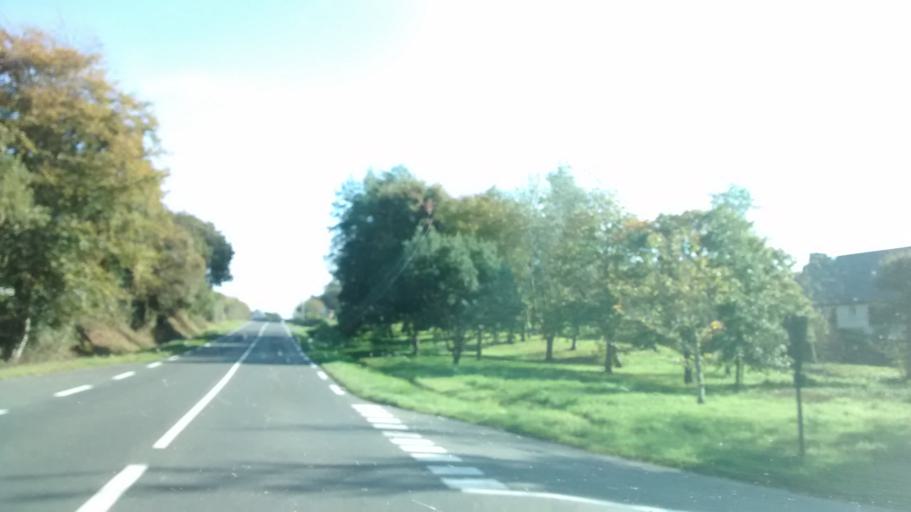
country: FR
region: Brittany
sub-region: Departement des Cotes-d'Armor
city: Pleumeur-Bodou
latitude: 48.7582
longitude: -3.5324
